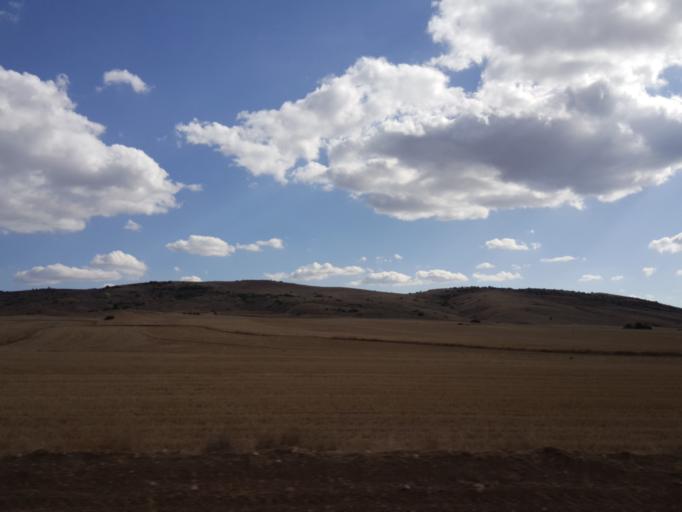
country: TR
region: Tokat
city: Sulusaray
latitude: 39.9865
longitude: 35.9591
